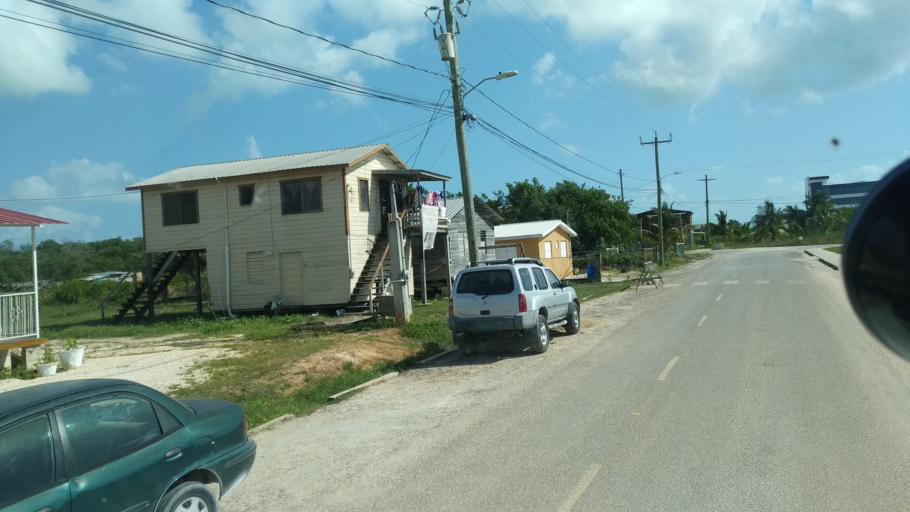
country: BZ
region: Belize
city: Belize City
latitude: 17.5169
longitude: -88.2341
